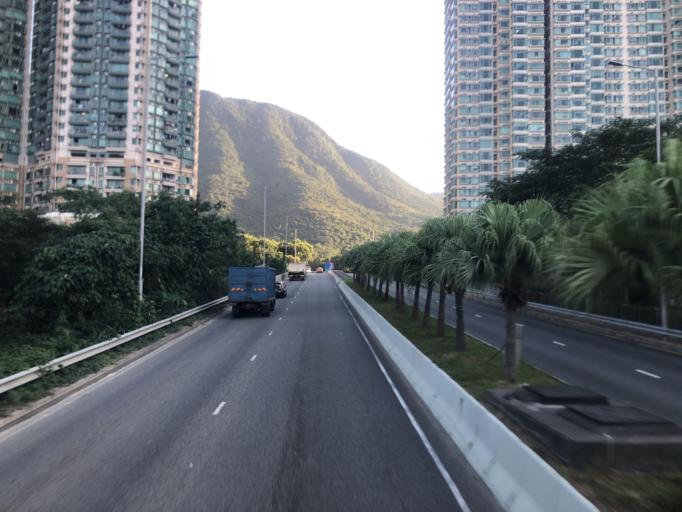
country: HK
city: Tai O
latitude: 22.2925
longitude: 113.9472
